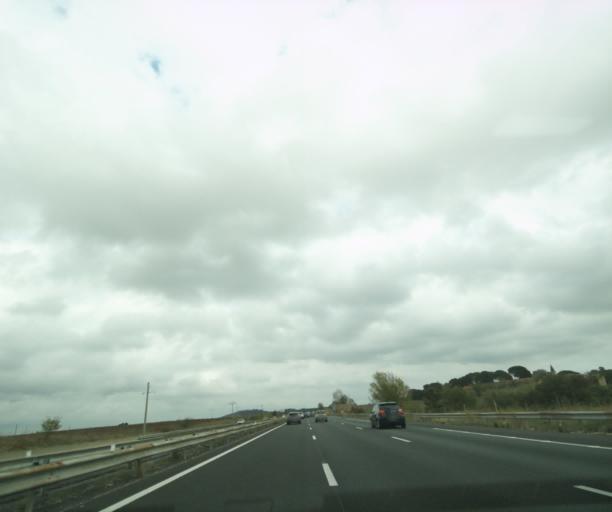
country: FR
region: Languedoc-Roussillon
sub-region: Departement de l'Herault
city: Bessan
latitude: 43.3694
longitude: 3.3934
